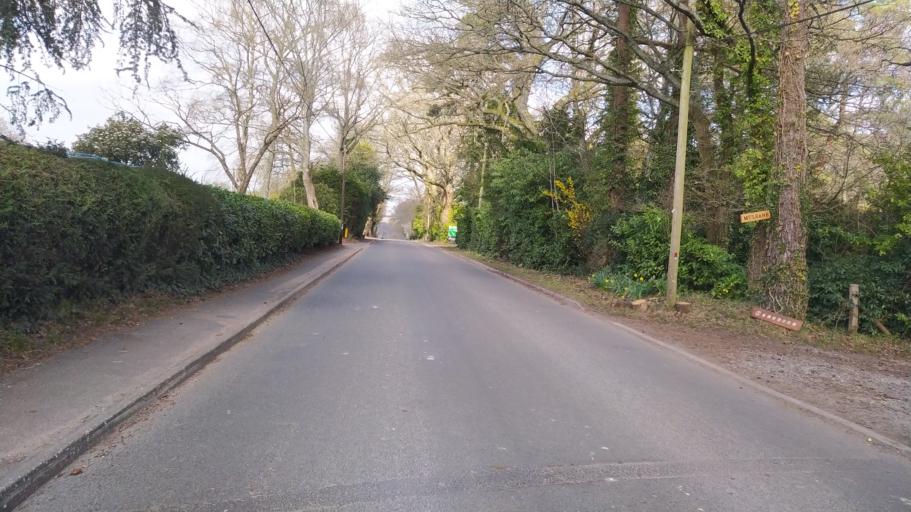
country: GB
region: England
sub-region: Hampshire
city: West Wellow
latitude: 50.9684
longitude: -1.5625
